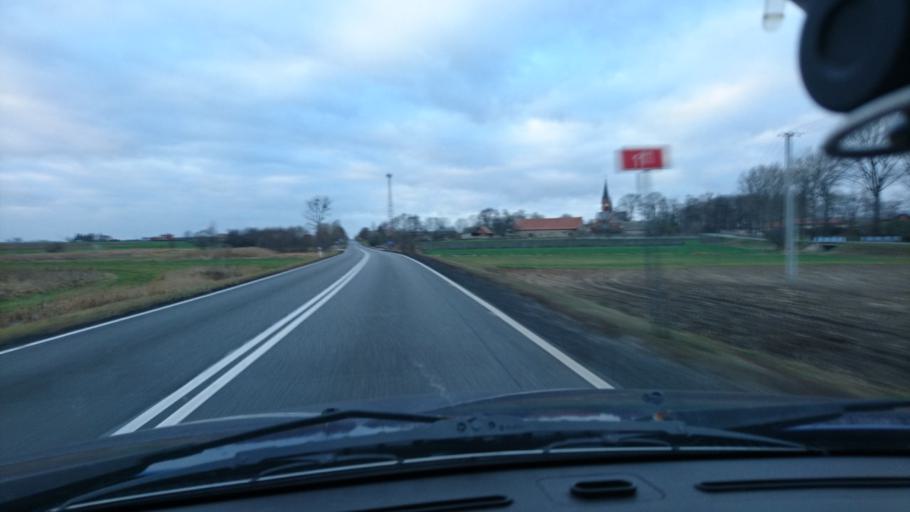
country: PL
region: Greater Poland Voivodeship
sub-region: Powiat kepinski
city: Opatow
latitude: 51.2090
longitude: 18.1464
